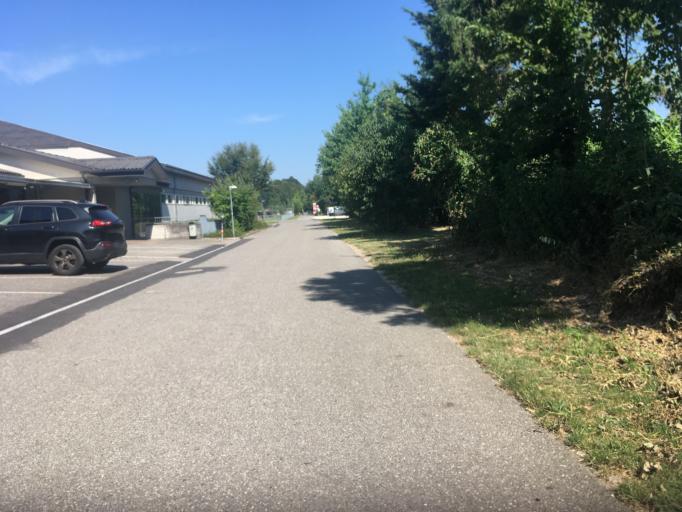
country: CH
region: Bern
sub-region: Emmental District
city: Kirchberg
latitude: 47.0871
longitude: 7.5776
